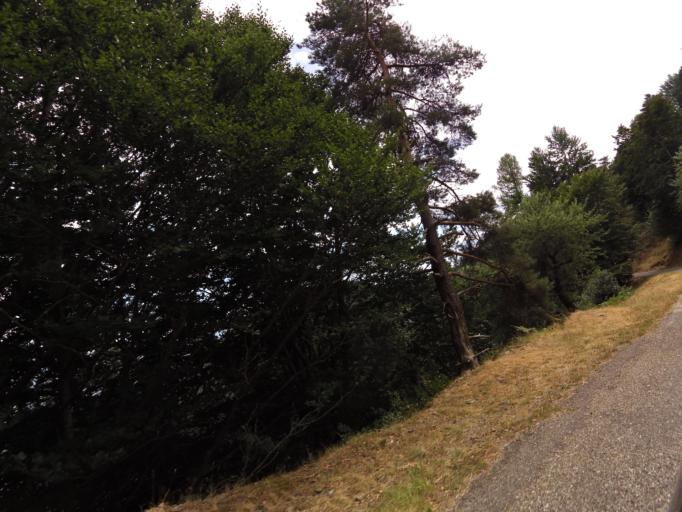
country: FR
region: Languedoc-Roussillon
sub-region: Departement du Gard
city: Valleraugue
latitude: 44.0525
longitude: 3.6061
